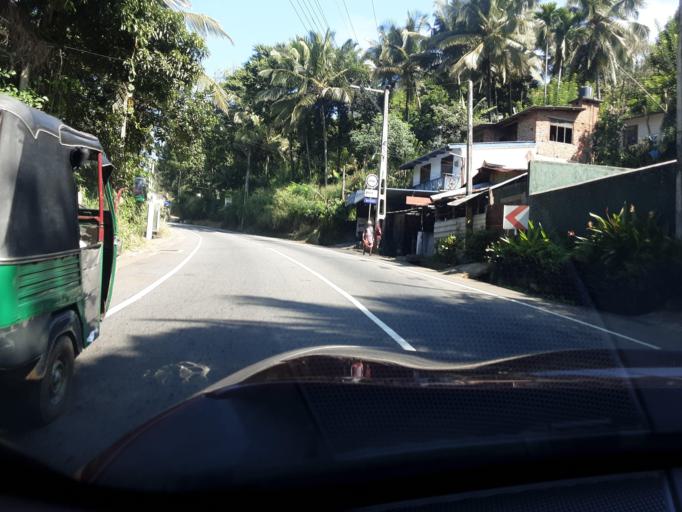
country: LK
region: Uva
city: Badulla
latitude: 7.0105
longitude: 81.0564
